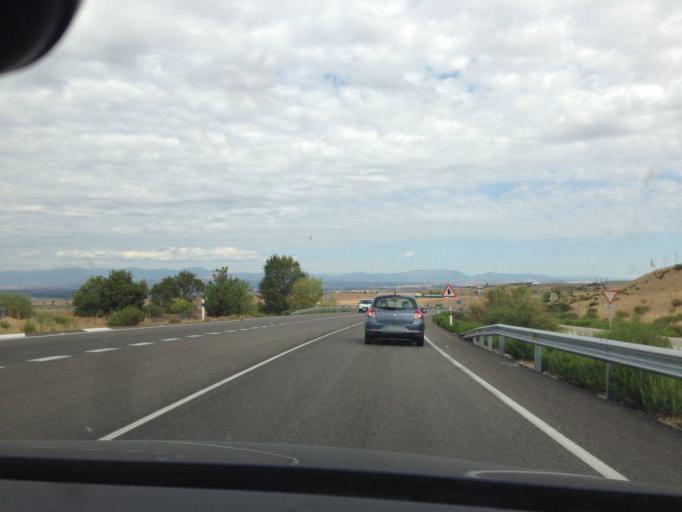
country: ES
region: Madrid
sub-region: Provincia de Madrid
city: Cobena
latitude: 40.5598
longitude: -3.5158
